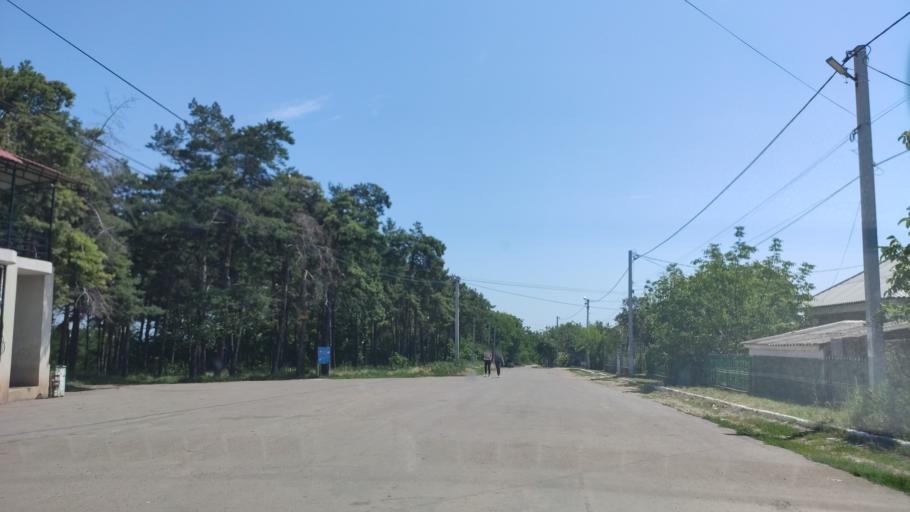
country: MD
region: Raionul Soroca
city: Soroca
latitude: 48.1453
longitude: 28.2894
